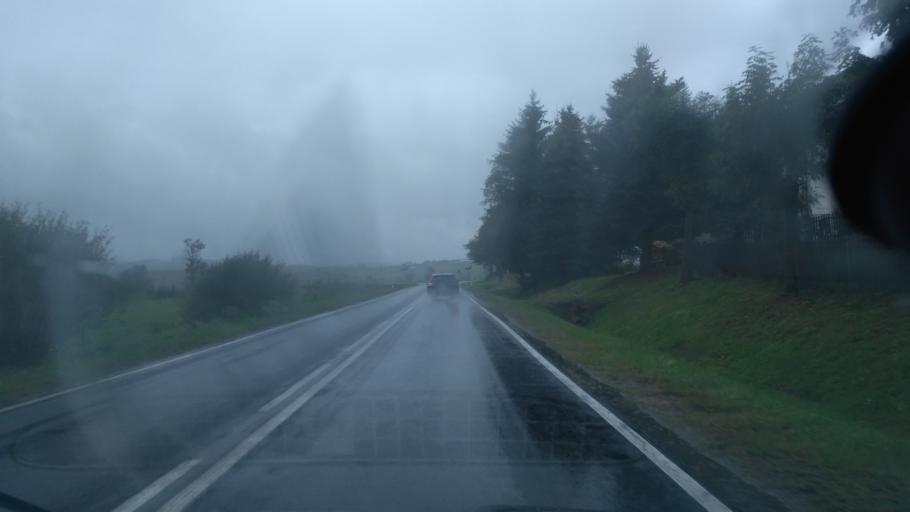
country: PL
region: Subcarpathian Voivodeship
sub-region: Powiat ropczycko-sedziszowski
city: Niedzwiada
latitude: 49.9757
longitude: 21.5664
